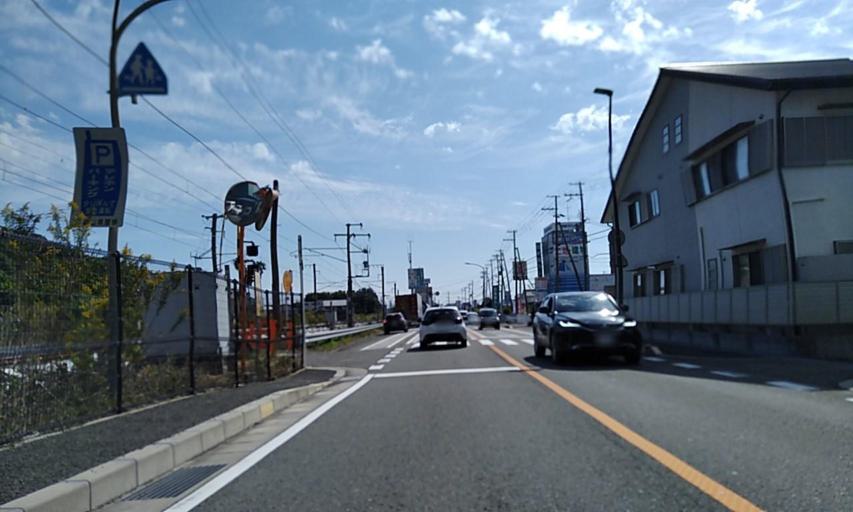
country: JP
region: Wakayama
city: Gobo
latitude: 33.9130
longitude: 135.1490
